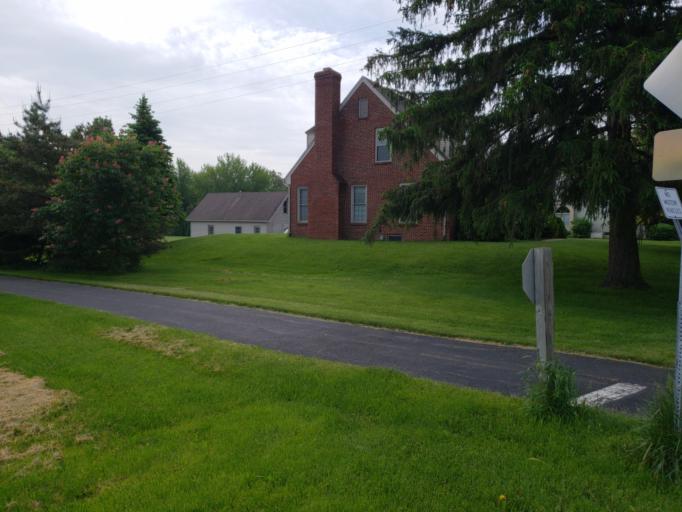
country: US
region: Ohio
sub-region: Lucas County
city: Waterville
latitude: 41.4938
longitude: -83.7196
